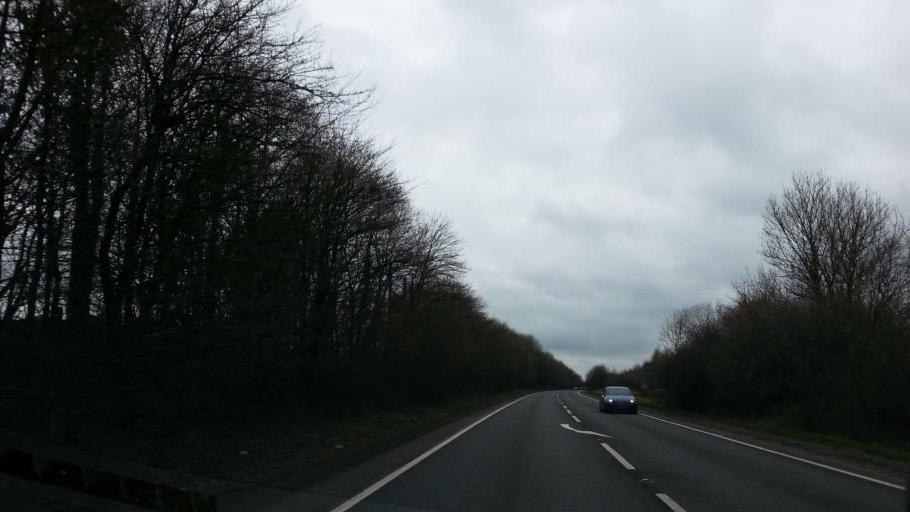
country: GB
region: England
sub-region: Devon
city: South Molton
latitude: 51.0289
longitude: -3.8288
